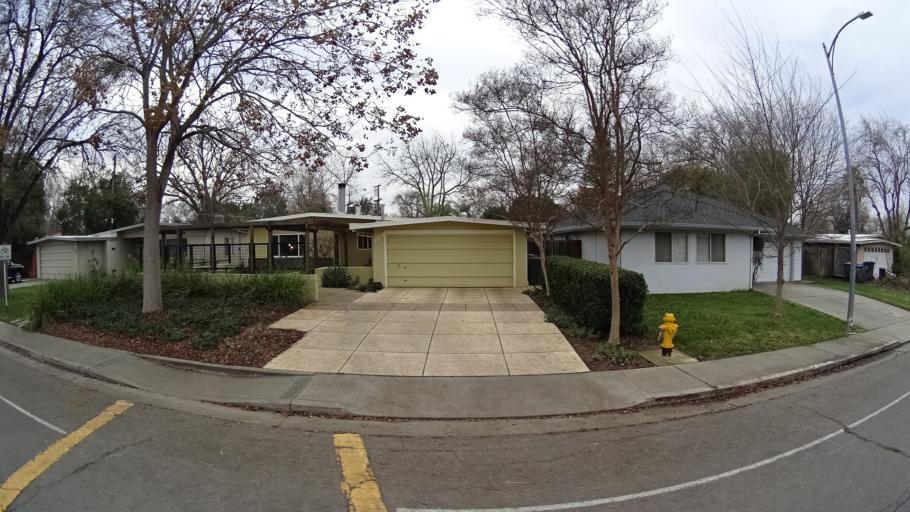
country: US
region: California
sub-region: Yolo County
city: Davis
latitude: 38.5584
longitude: -121.7286
